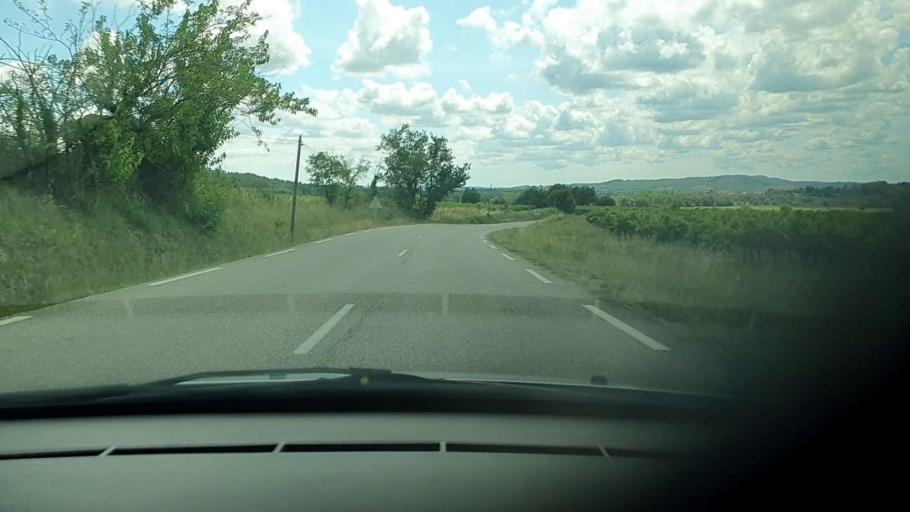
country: FR
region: Languedoc-Roussillon
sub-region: Departement du Gard
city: Moussac
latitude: 44.0048
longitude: 4.2266
